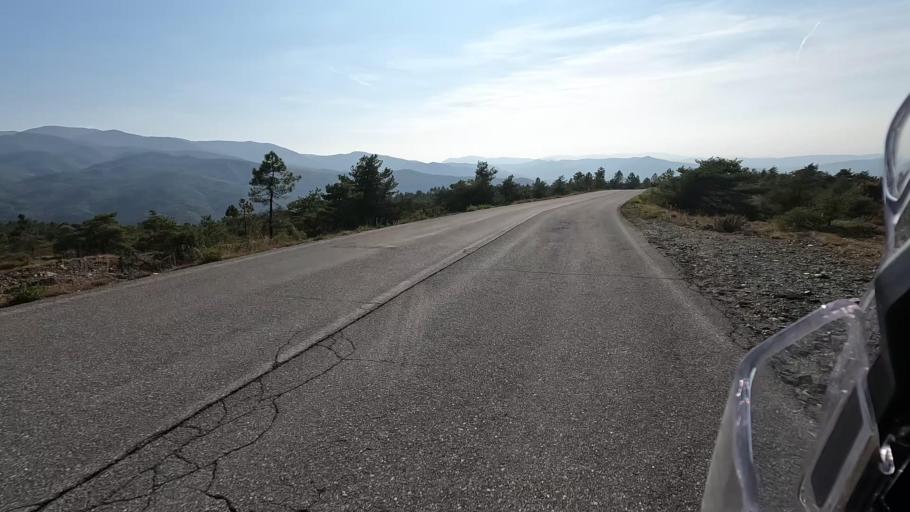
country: IT
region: Liguria
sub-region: Provincia di Savona
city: Urbe
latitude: 44.5081
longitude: 8.5387
